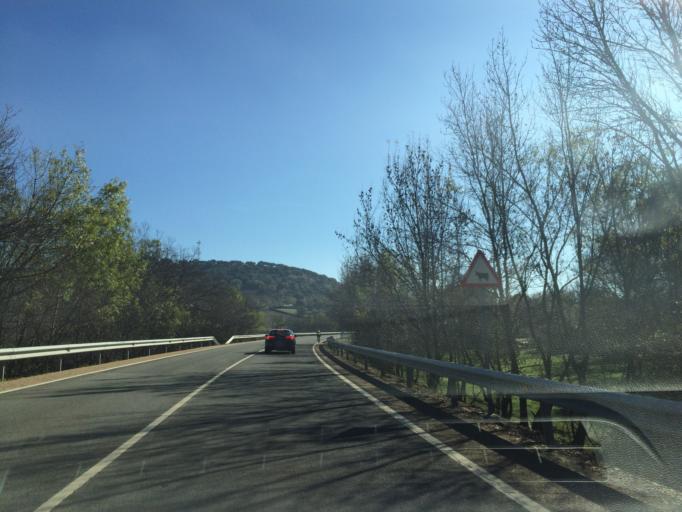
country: ES
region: Madrid
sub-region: Provincia de Madrid
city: Guadalix de la Sierra
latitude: 40.7930
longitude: -3.6884
